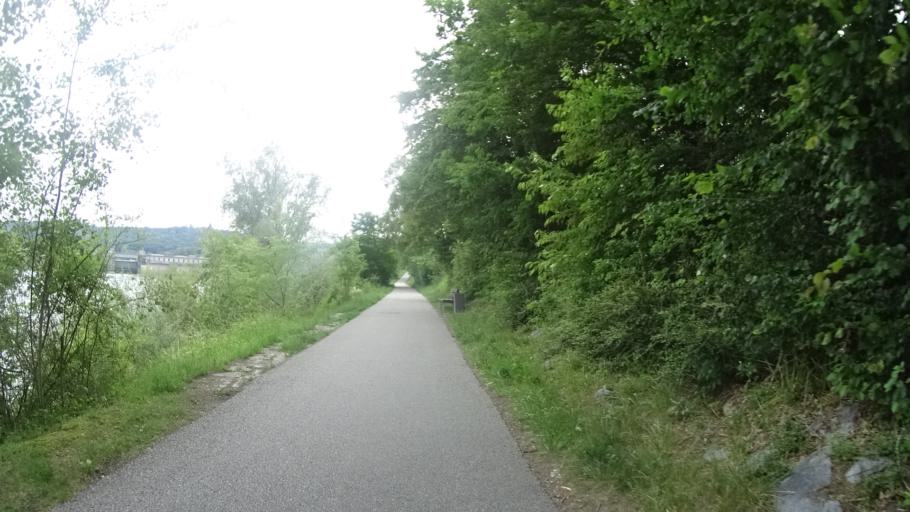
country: DE
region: Bavaria
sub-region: Lower Bavaria
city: Passau
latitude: 48.5580
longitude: 13.4366
